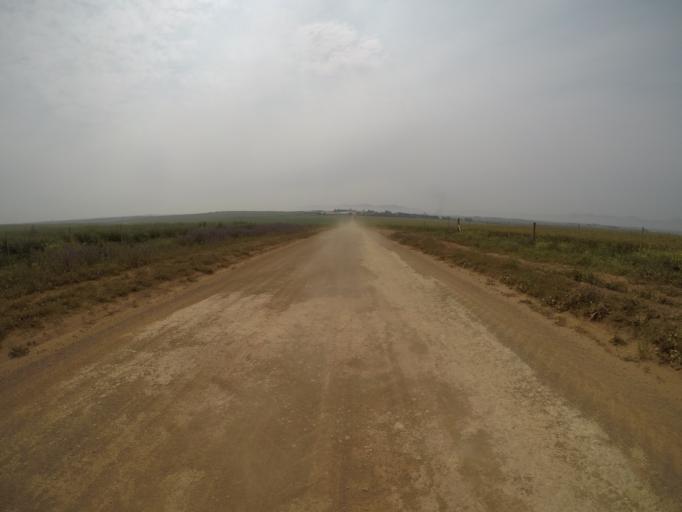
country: ZA
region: Western Cape
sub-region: City of Cape Town
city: Kraaifontein
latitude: -33.7148
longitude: 18.6835
